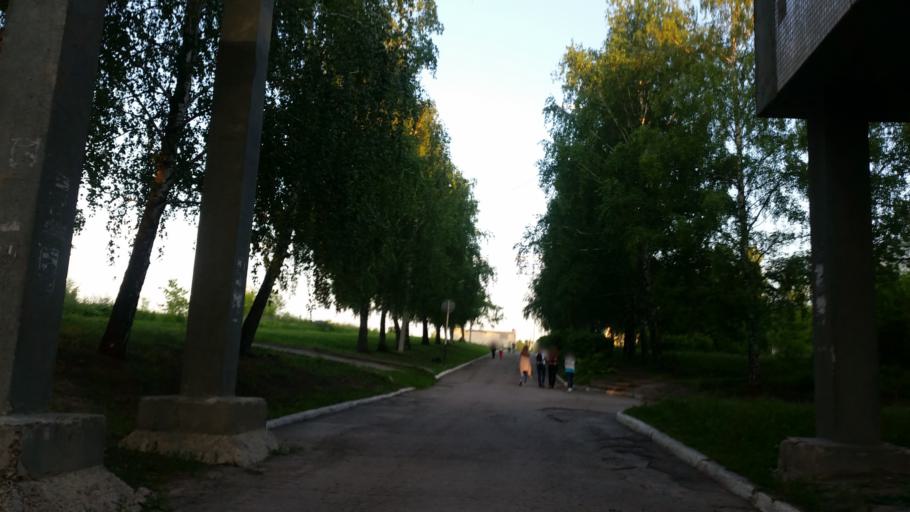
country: RU
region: Ulyanovsk
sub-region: Ulyanovskiy Rayon
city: Ulyanovsk
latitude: 54.3532
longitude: 48.3894
